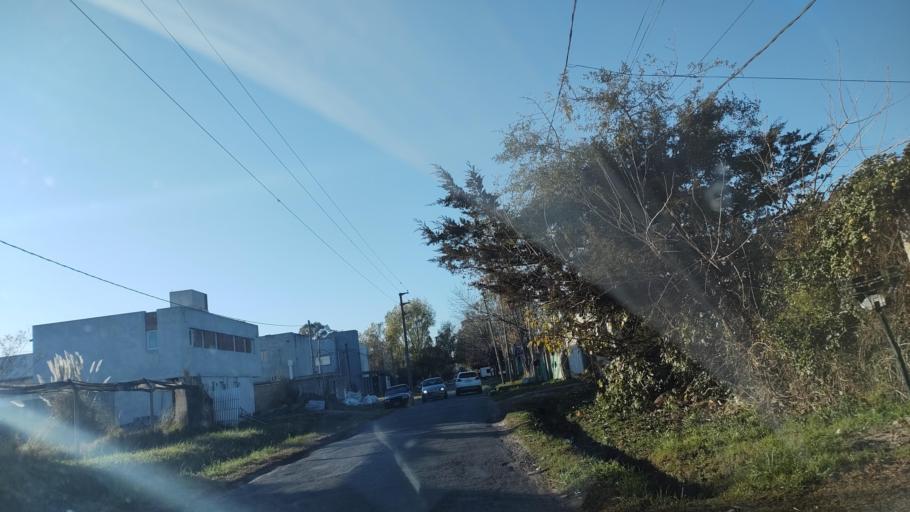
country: AR
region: Buenos Aires
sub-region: Partido de La Plata
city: La Plata
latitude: -34.8849
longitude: -58.0699
